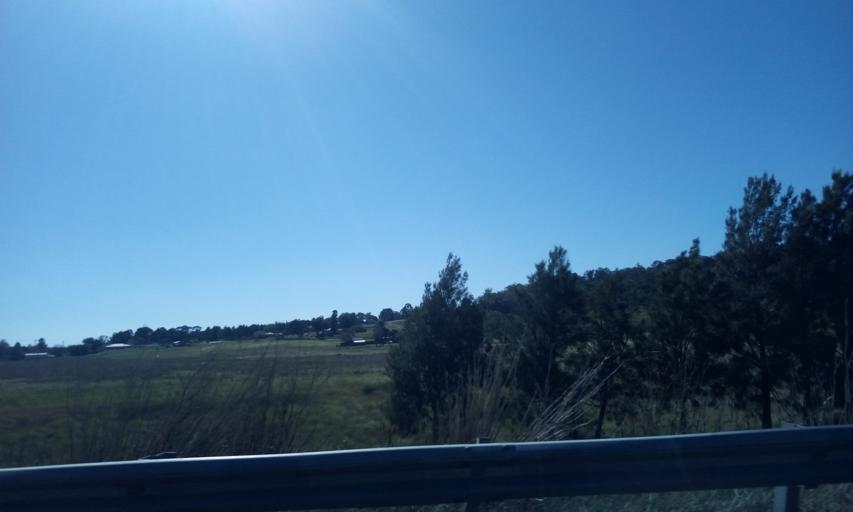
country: AU
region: New South Wales
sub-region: Goulburn Mulwaree
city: Goulburn
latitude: -34.7769
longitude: 149.7268
